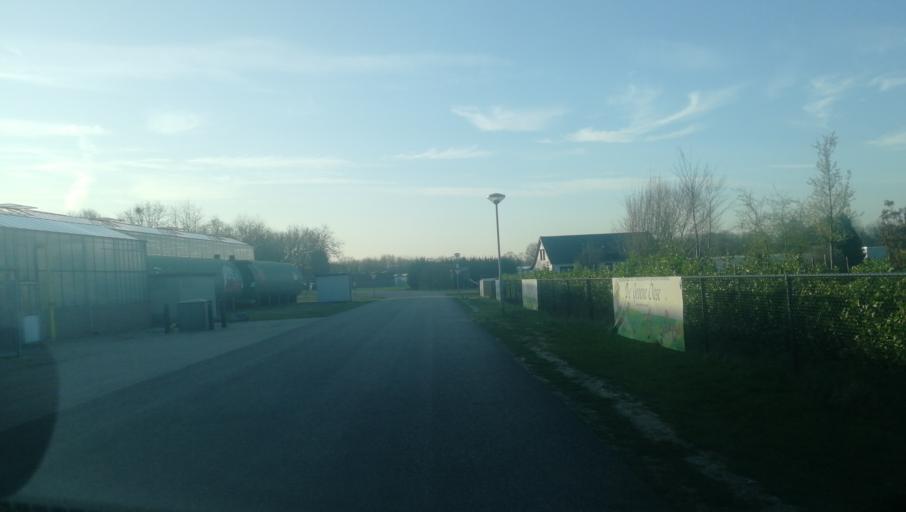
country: NL
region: Limburg
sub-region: Gemeente Venlo
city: Venlo
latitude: 51.3523
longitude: 6.1958
